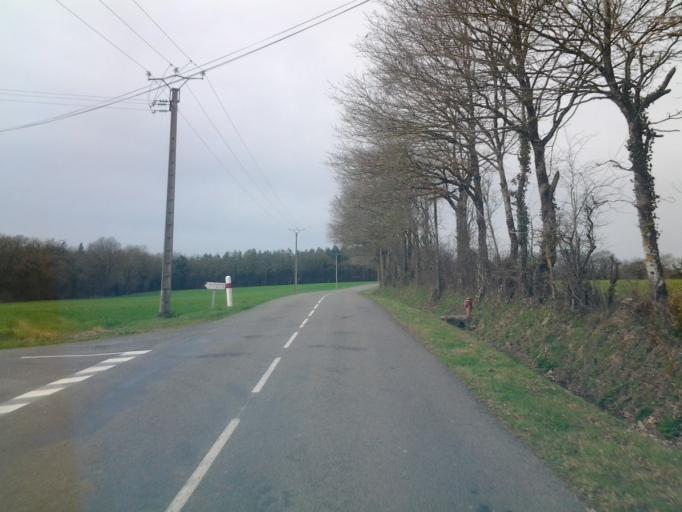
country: FR
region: Pays de la Loire
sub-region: Departement de la Vendee
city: Venansault
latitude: 46.6873
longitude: -1.5346
